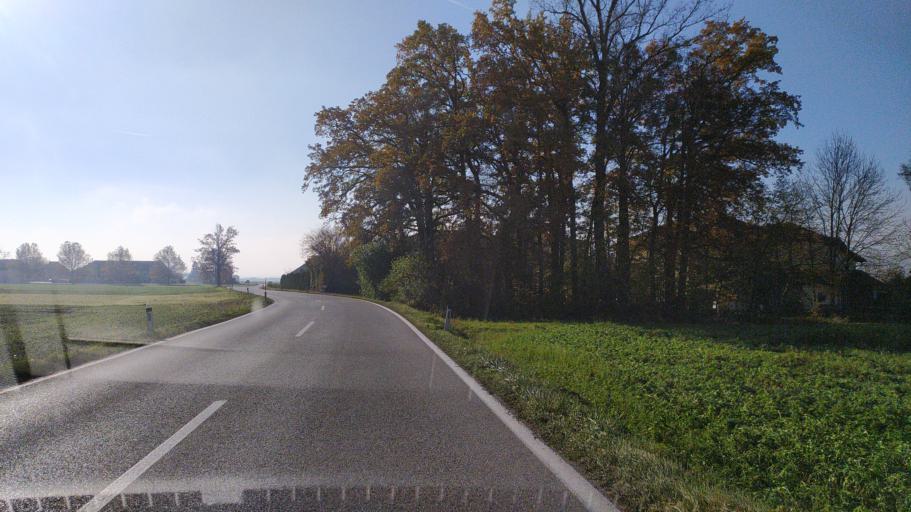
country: AT
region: Upper Austria
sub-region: Politischer Bezirk Perg
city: Perg
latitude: 48.2340
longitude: 14.6227
